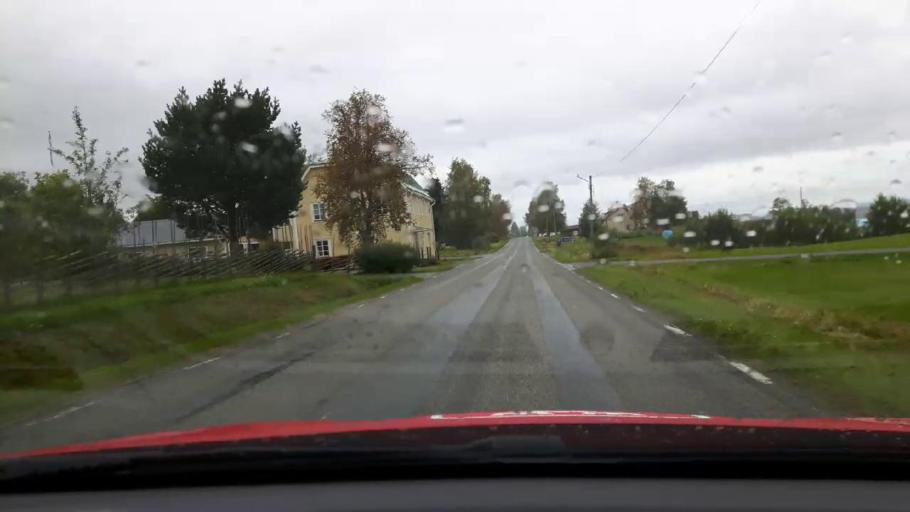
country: SE
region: Jaemtland
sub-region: Bergs Kommun
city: Hoverberg
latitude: 62.8456
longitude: 14.3832
